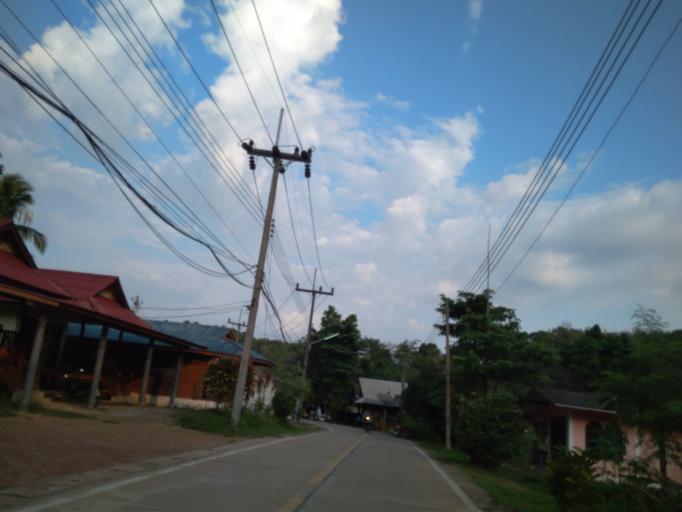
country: TH
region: Phangnga
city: Ko Yao
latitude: 8.1369
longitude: 98.6231
